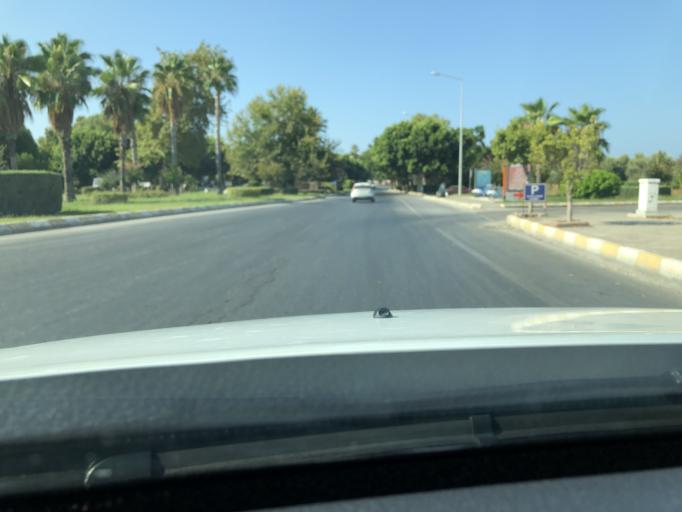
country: TR
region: Antalya
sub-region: Manavgat
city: Side
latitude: 36.7763
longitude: 31.3969
